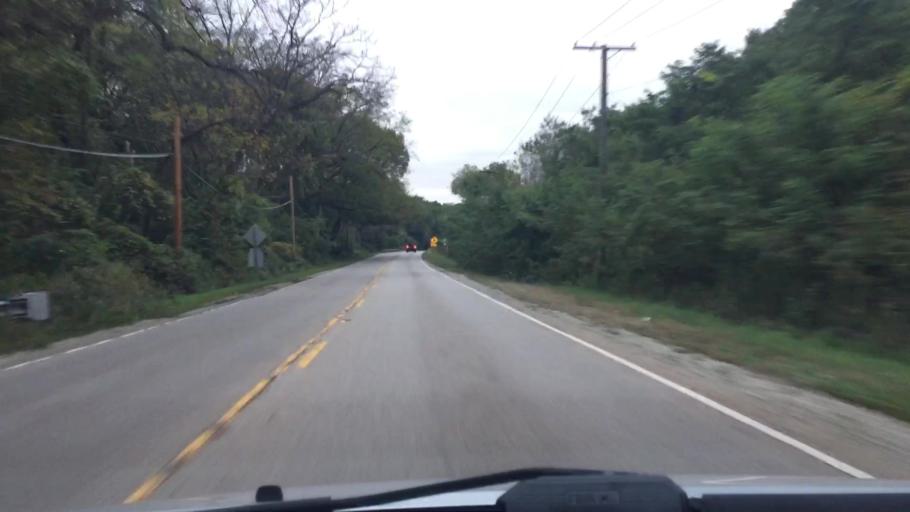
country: US
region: Illinois
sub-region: Kane County
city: Sleepy Hollow
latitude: 42.1180
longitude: -88.2978
